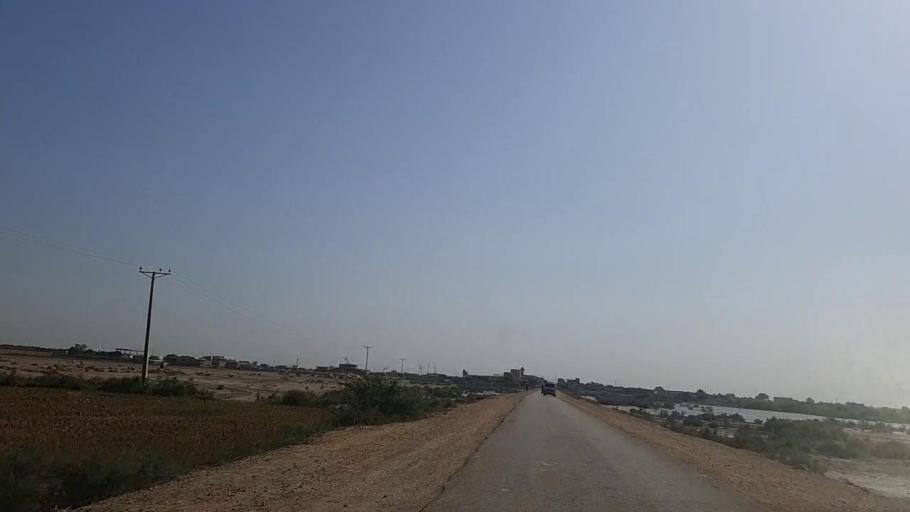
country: PK
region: Sindh
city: Mirpur Batoro
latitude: 24.6231
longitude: 68.2948
